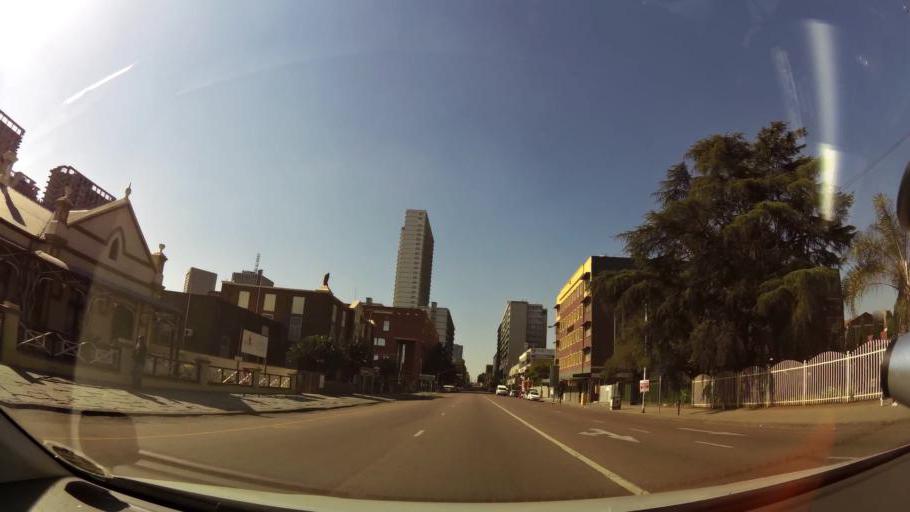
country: ZA
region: Gauteng
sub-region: City of Tshwane Metropolitan Municipality
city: Pretoria
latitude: -25.7469
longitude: 28.1815
